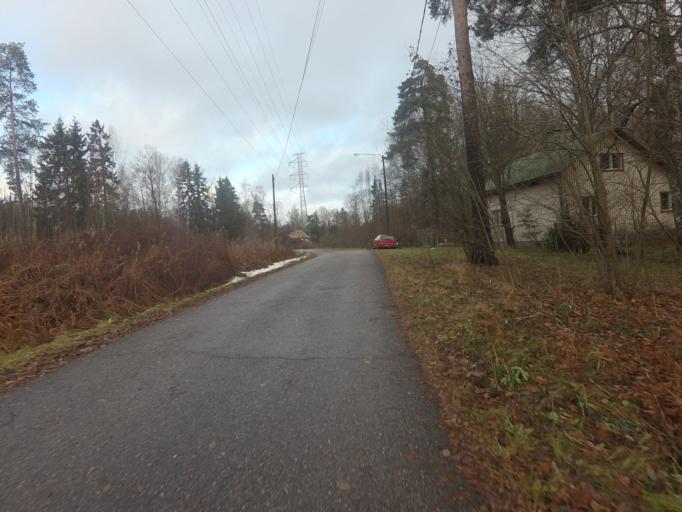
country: FI
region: Uusimaa
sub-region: Helsinki
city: Otaniemi
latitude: 60.1966
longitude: 24.8075
